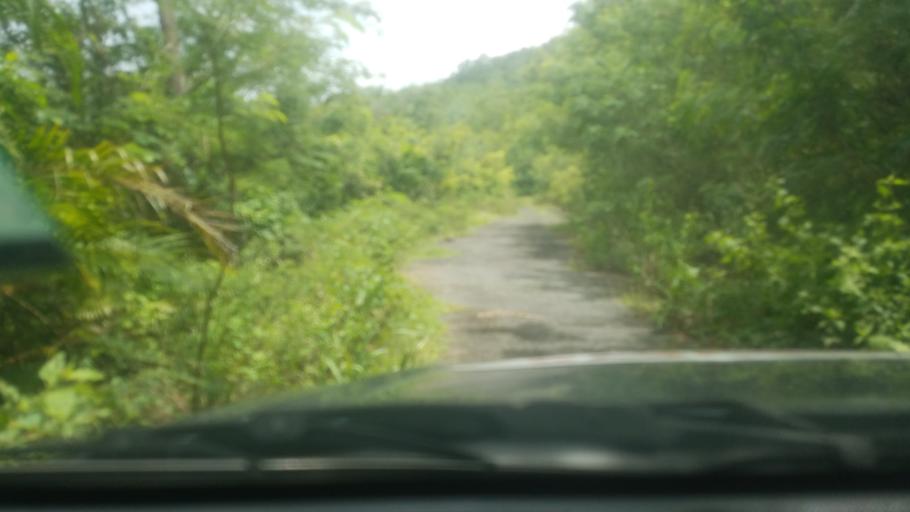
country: LC
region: Laborie Quarter
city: Laborie
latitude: 13.7579
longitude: -61.0002
